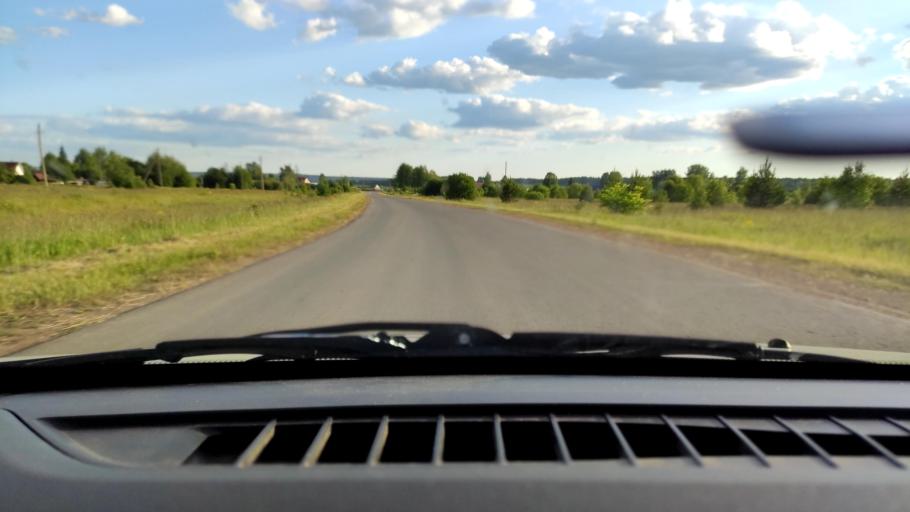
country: RU
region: Perm
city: Uinskoye
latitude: 57.0983
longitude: 56.6452
